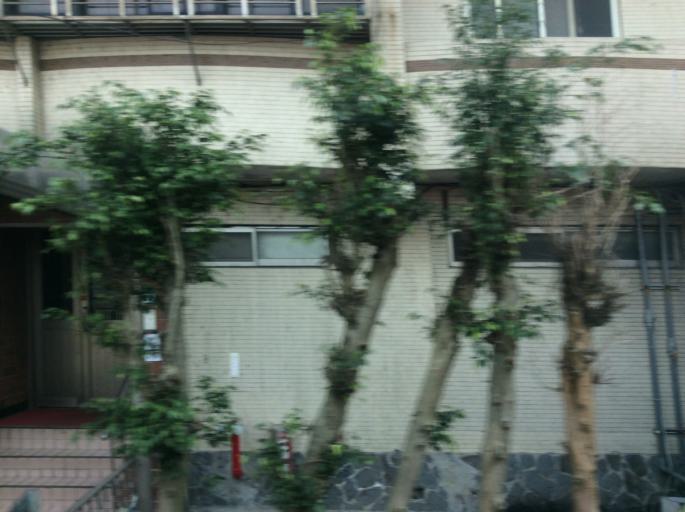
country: TW
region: Taipei
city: Taipei
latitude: 25.1424
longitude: 121.5495
